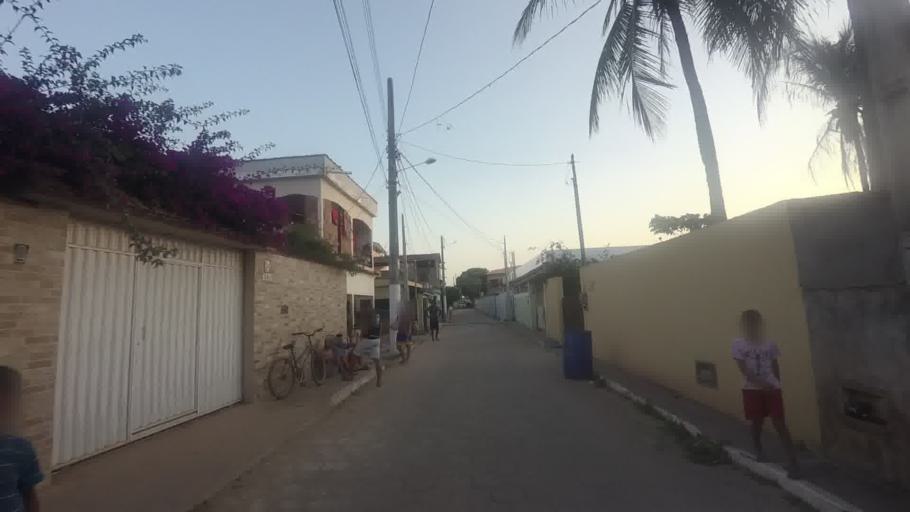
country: BR
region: Espirito Santo
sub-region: Piuma
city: Piuma
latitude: -20.8908
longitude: -40.7756
